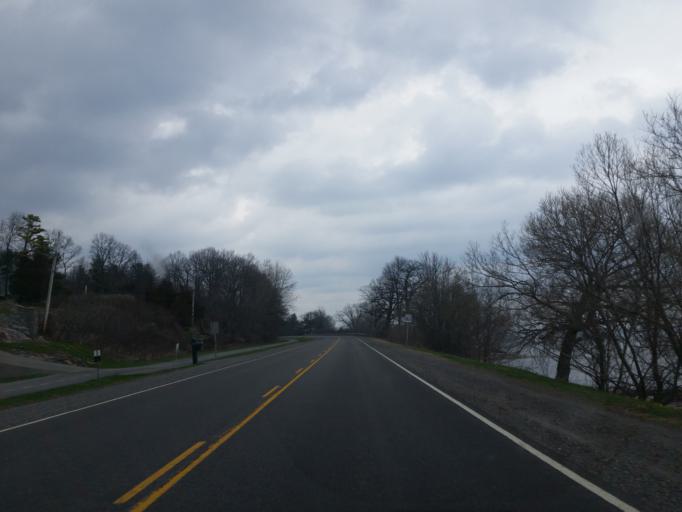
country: US
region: New York
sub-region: Jefferson County
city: Alexandria Bay
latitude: 44.4702
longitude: -75.8396
